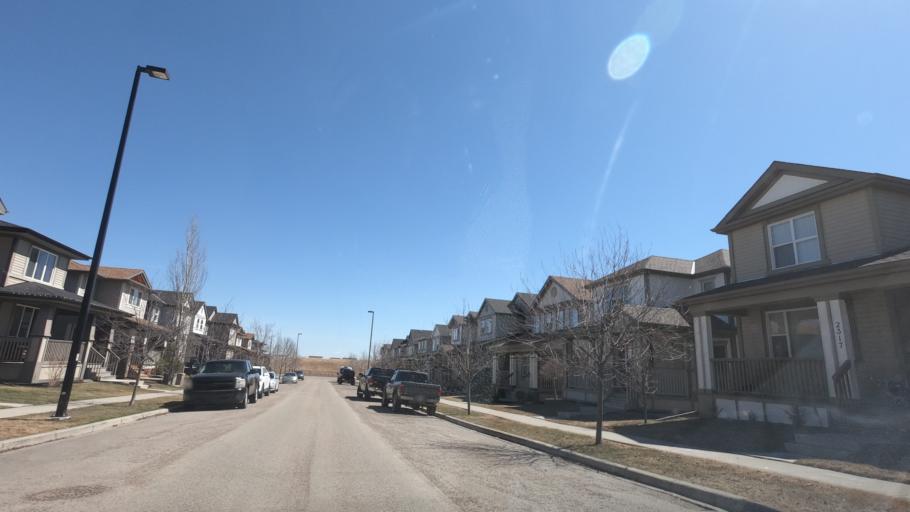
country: CA
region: Alberta
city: Airdrie
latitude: 51.3039
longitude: -114.0451
